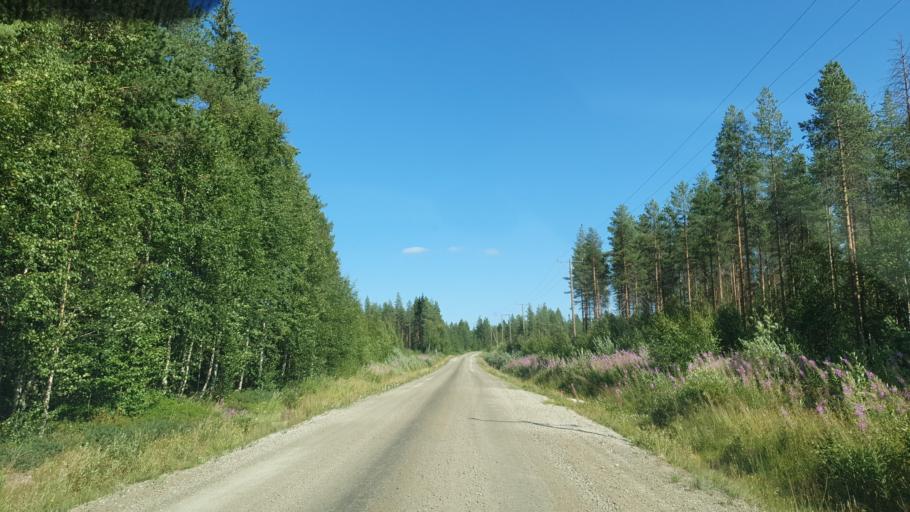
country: FI
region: Kainuu
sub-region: Kehys-Kainuu
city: Kuhmo
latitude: 64.0476
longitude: 29.6401
